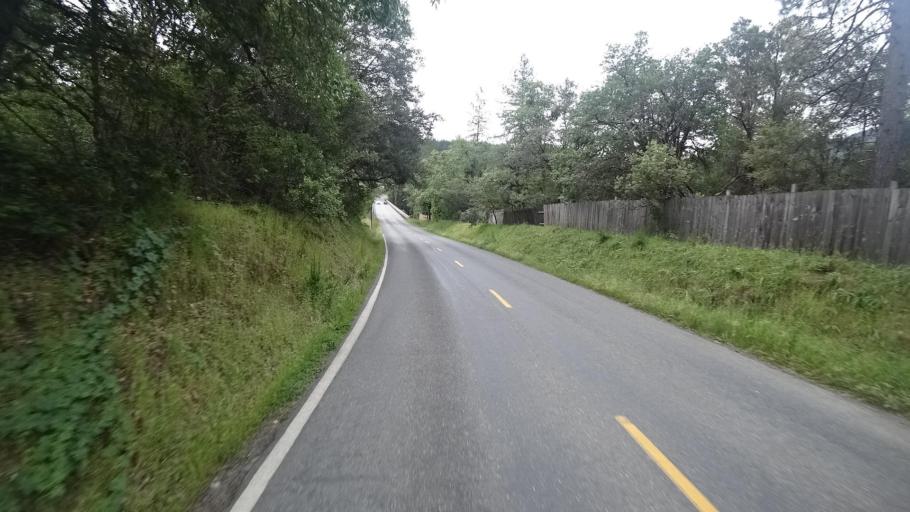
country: US
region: California
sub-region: Humboldt County
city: Willow Creek
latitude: 40.9472
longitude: -123.6253
